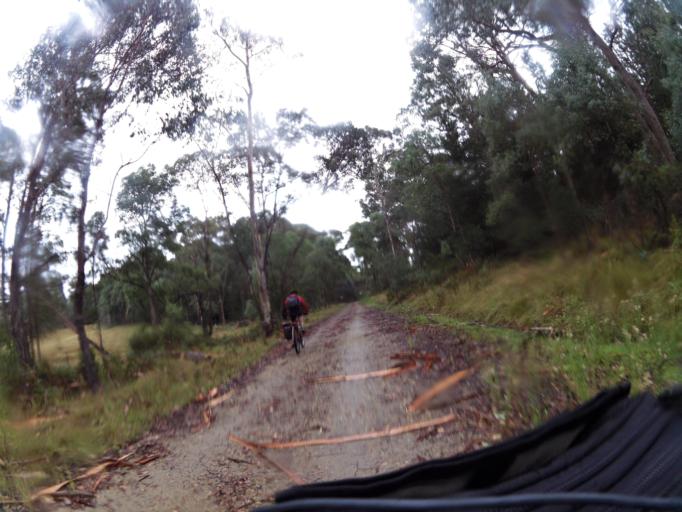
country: AU
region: New South Wales
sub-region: Greater Hume Shire
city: Holbrook
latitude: -36.1734
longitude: 147.4985
